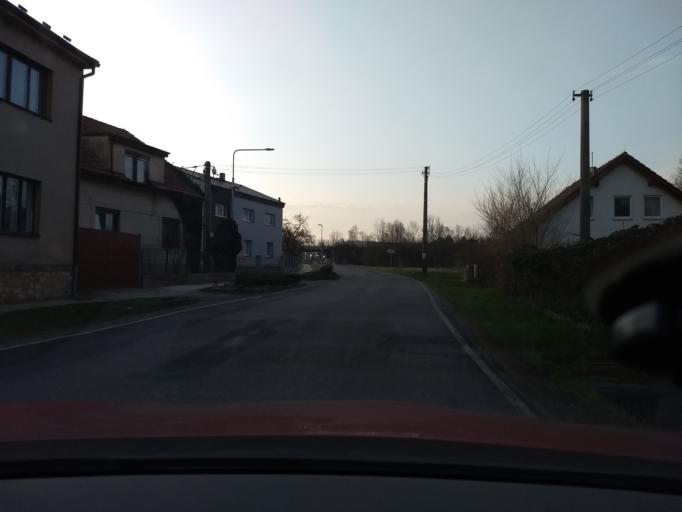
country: CZ
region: Central Bohemia
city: Rudna
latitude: 50.0301
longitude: 14.2065
